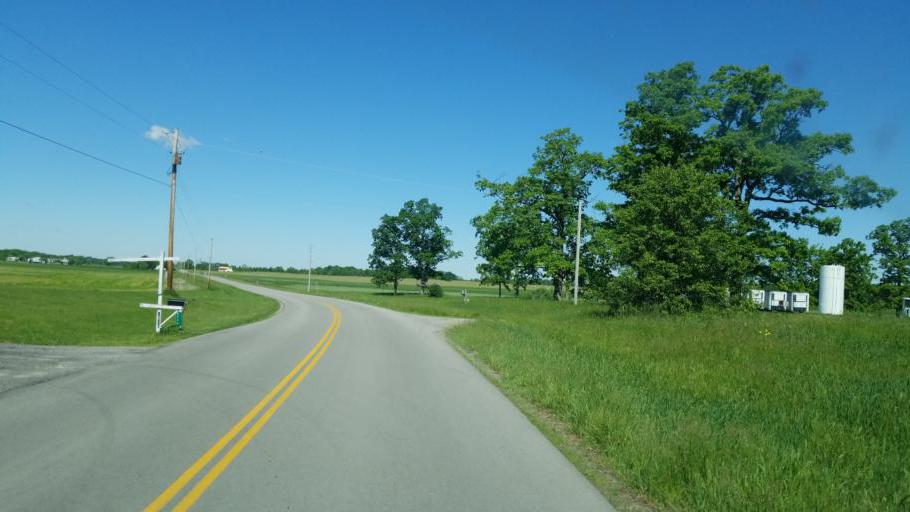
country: US
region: Ohio
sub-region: Logan County
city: Russells Point
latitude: 40.4247
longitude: -83.8573
